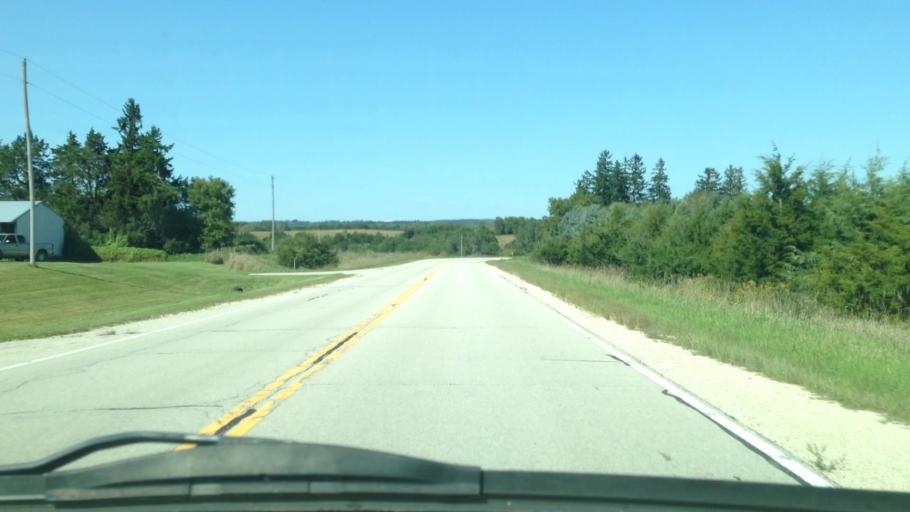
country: US
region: Minnesota
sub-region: Fillmore County
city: Rushford
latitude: 43.6394
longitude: -91.7903
